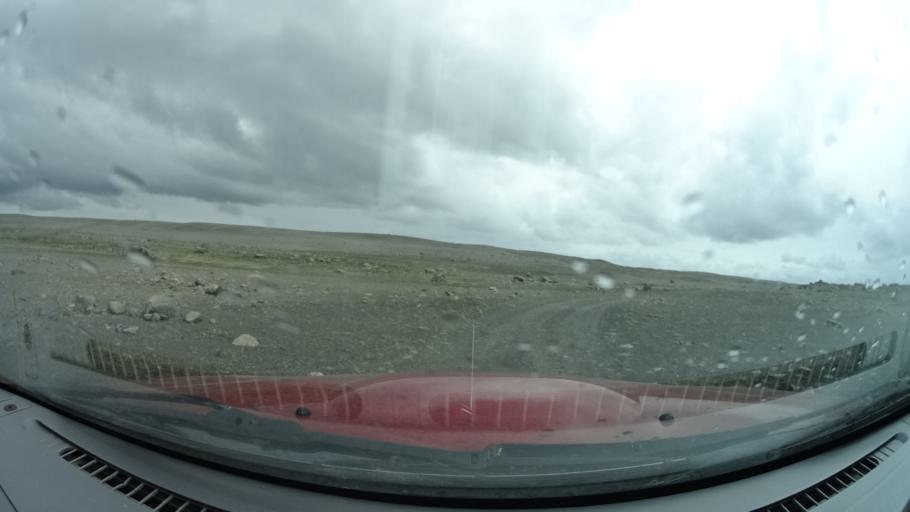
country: IS
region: Northeast
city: Laugar
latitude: 65.7662
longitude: -16.3513
